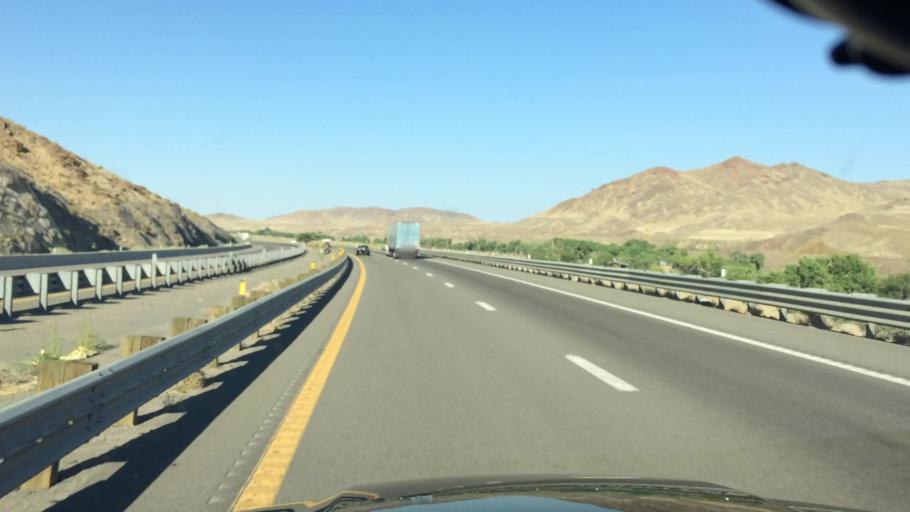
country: US
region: Nevada
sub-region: Lyon County
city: Fernley
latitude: 39.5982
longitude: -119.3508
